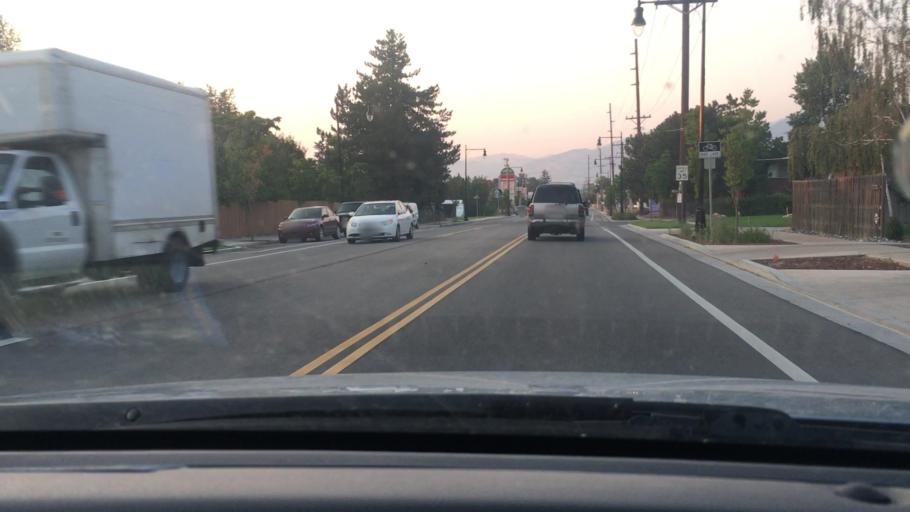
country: US
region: Utah
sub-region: Salt Lake County
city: Canyon Rim
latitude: 40.6971
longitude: -111.8244
